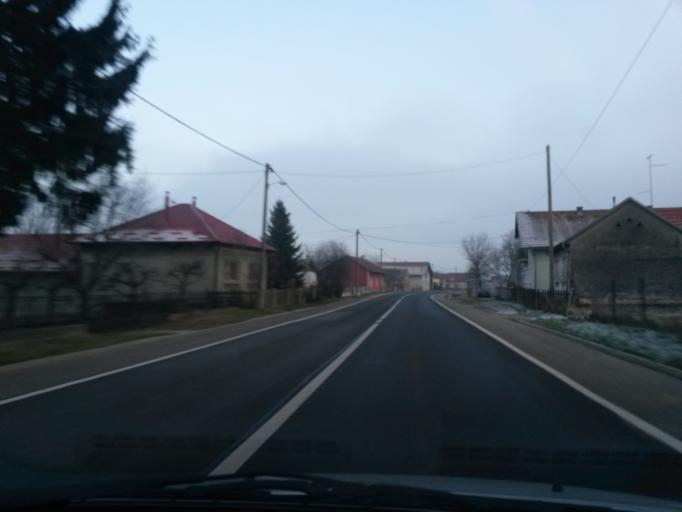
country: HR
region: Varazdinska
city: Ludbreg
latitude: 46.2112
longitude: 16.6947
